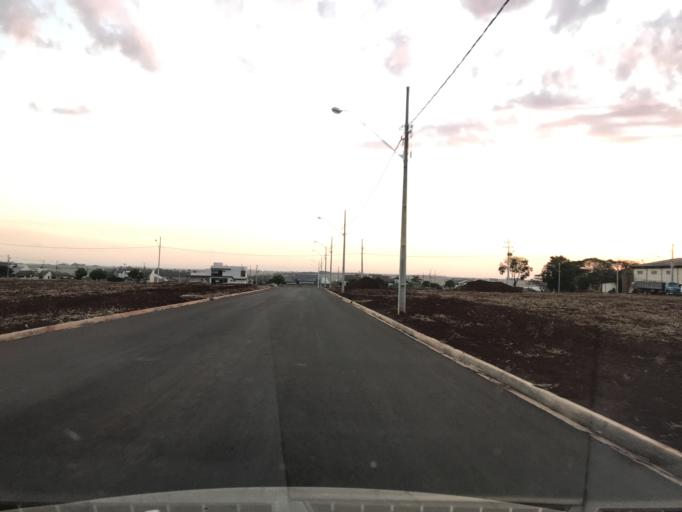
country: BR
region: Parana
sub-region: Palotina
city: Palotina
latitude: -24.3021
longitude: -53.8353
